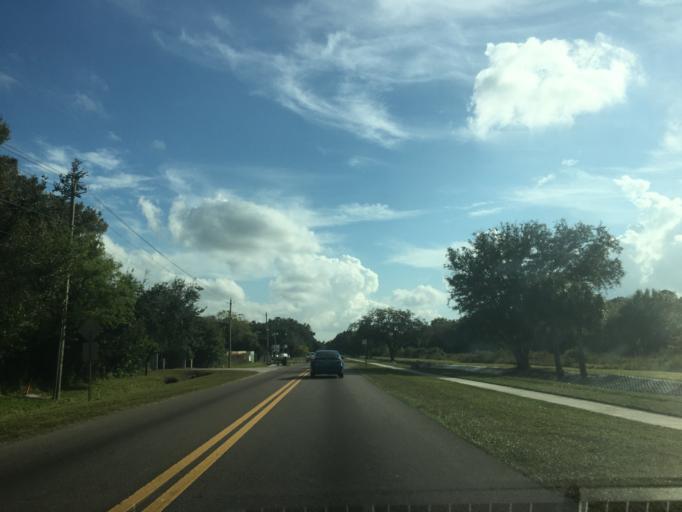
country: US
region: Florida
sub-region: Hillsborough County
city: Temple Terrace
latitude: 28.0167
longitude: -82.4319
